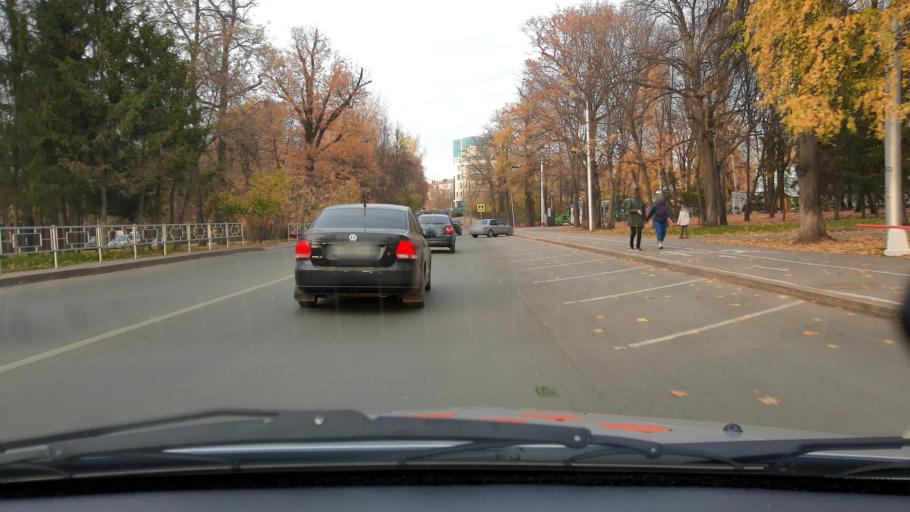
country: RU
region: Bashkortostan
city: Ufa
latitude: 54.7741
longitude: 56.0186
